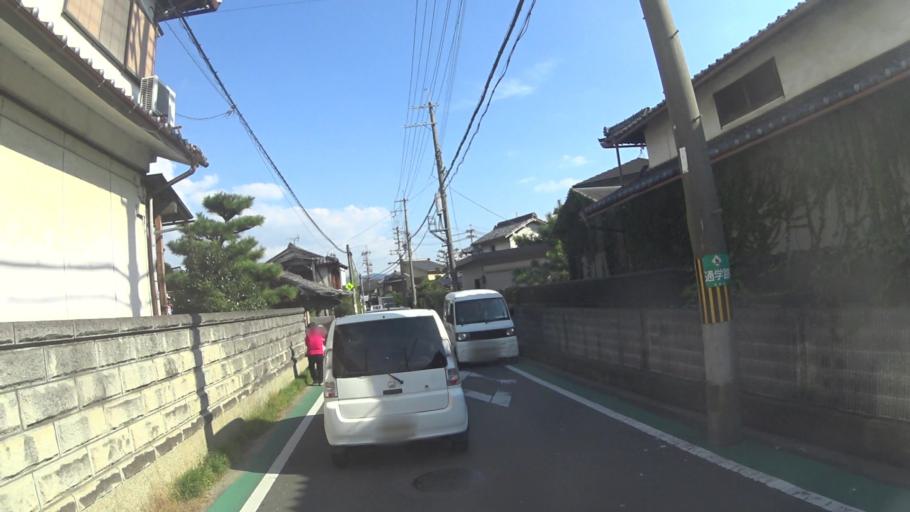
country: JP
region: Kyoto
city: Kameoka
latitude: 35.0254
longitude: 135.5626
